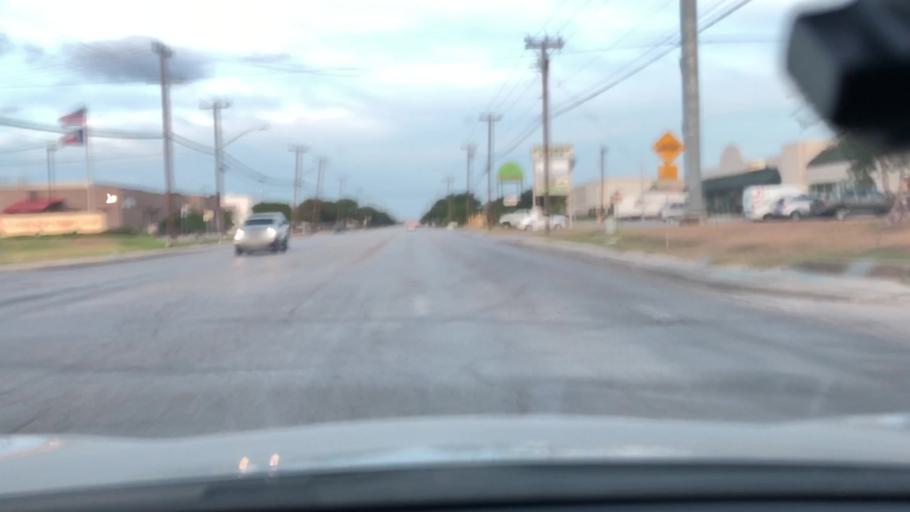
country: US
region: Texas
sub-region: Bexar County
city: Kirby
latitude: 29.4840
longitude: -98.3931
